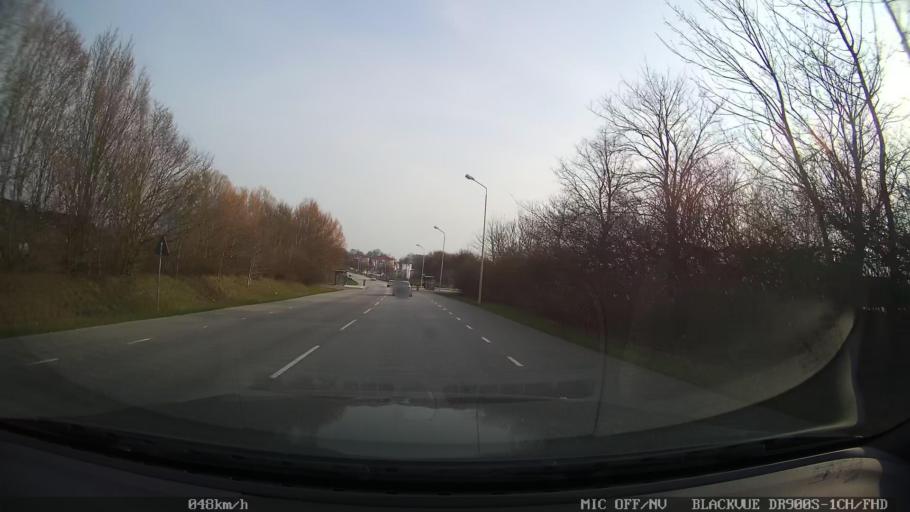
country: SE
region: Skane
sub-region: Ystads Kommun
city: Ystad
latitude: 55.4401
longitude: 13.8075
